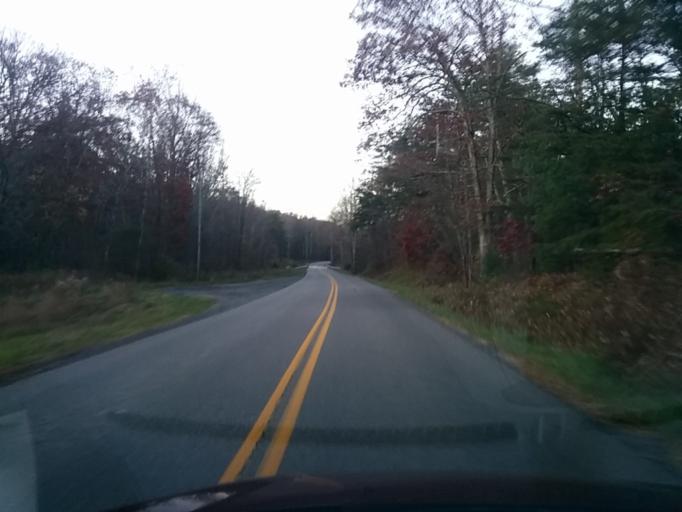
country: US
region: Virginia
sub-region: Rockbridge County
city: East Lexington
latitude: 37.9676
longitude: -79.5176
